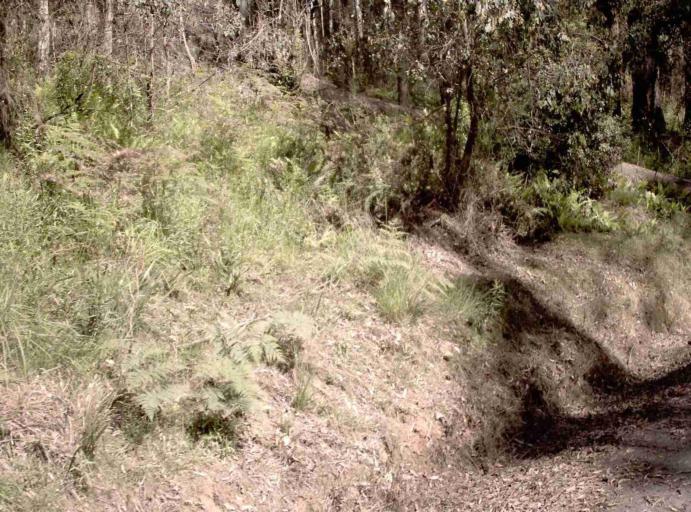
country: AU
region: New South Wales
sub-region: Bombala
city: Bombala
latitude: -37.2095
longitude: 148.7421
